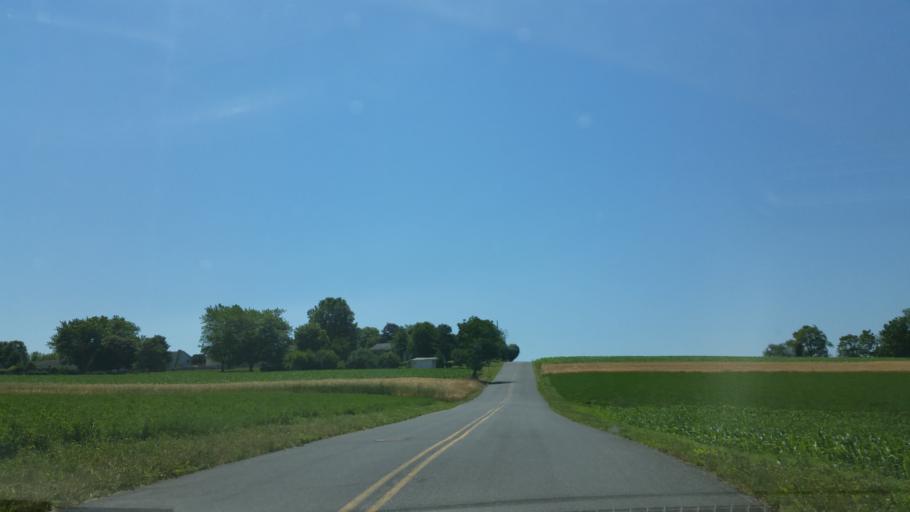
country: US
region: Pennsylvania
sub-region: Lebanon County
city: Fredericksburg
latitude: 40.4236
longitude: -76.4285
